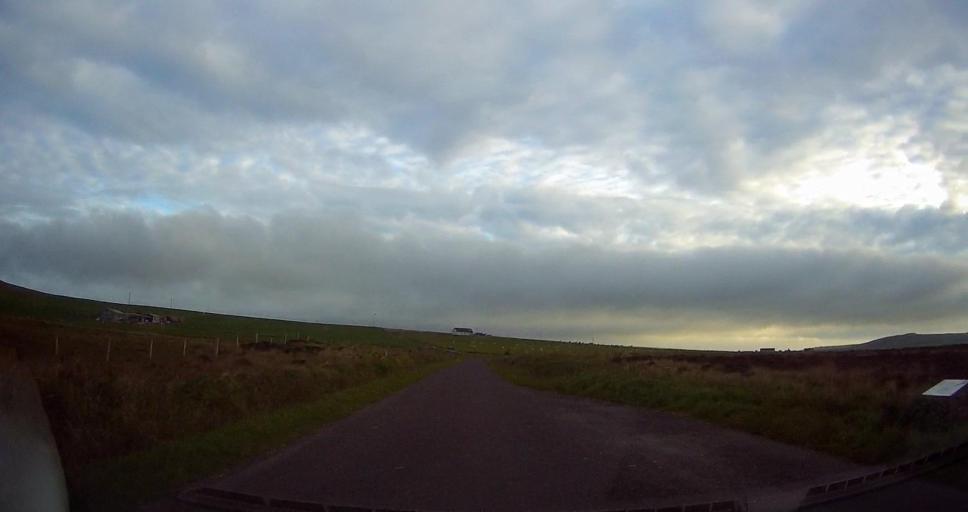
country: GB
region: Scotland
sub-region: Orkney Islands
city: Stromness
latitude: 59.1082
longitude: -3.2335
